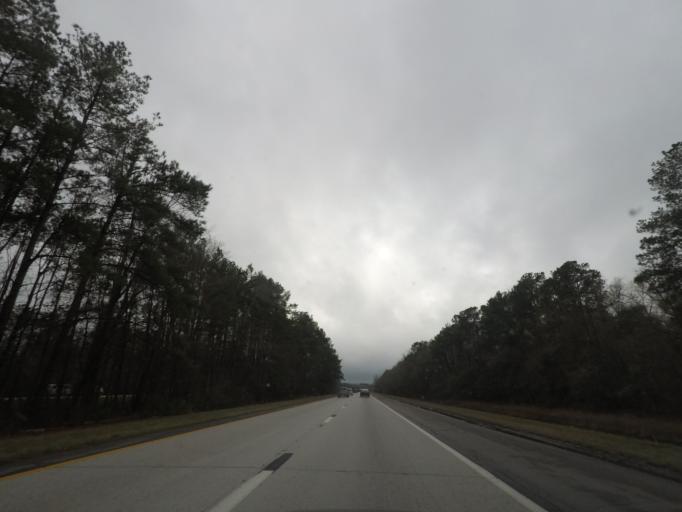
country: US
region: South Carolina
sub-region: Dorchester County
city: Saint George
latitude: 33.2468
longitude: -80.5802
